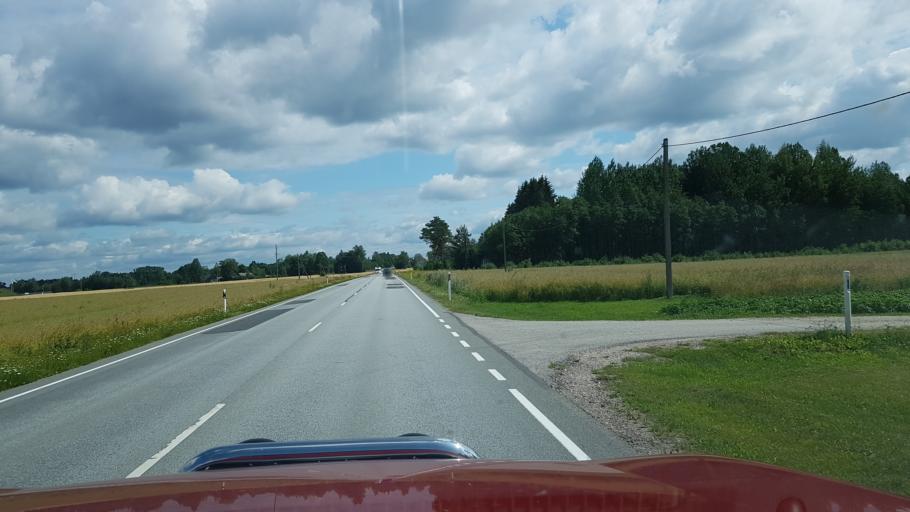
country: EE
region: Jogevamaa
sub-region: Jogeva linn
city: Jogeva
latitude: 58.8207
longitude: 26.5778
